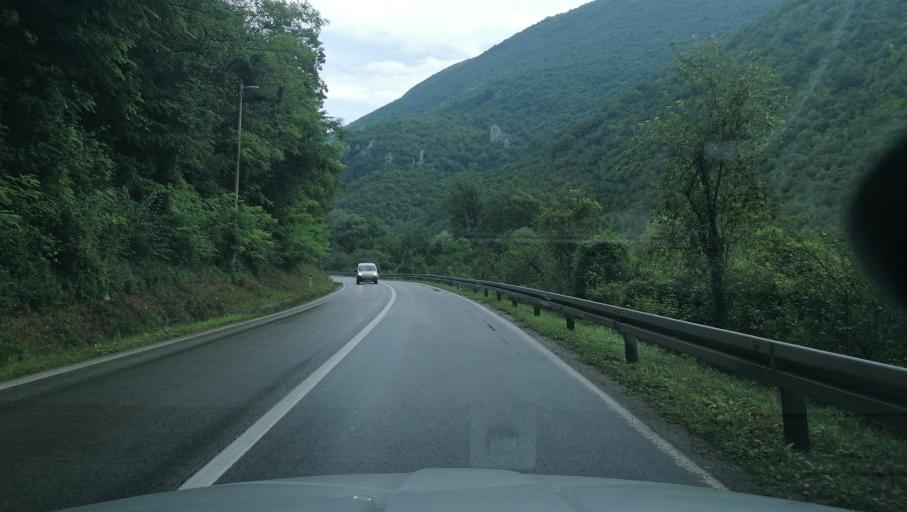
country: BA
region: Republika Srpska
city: Hiseti
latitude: 44.6421
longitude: 17.1464
